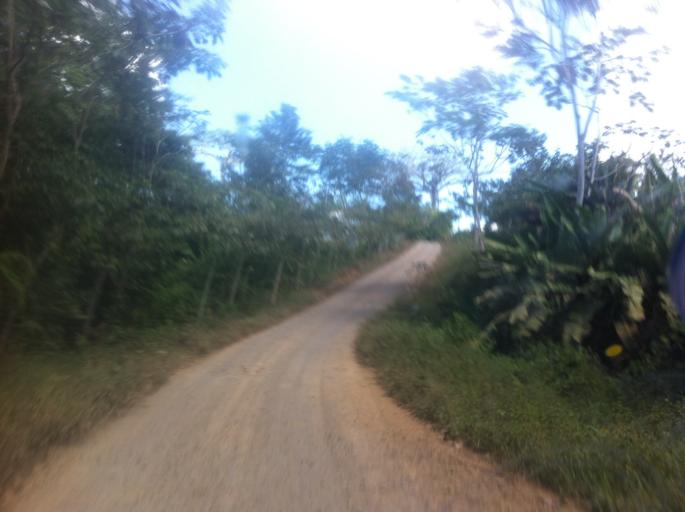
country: CR
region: Alajuela
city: Los Chiles
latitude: 11.2398
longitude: -84.4741
